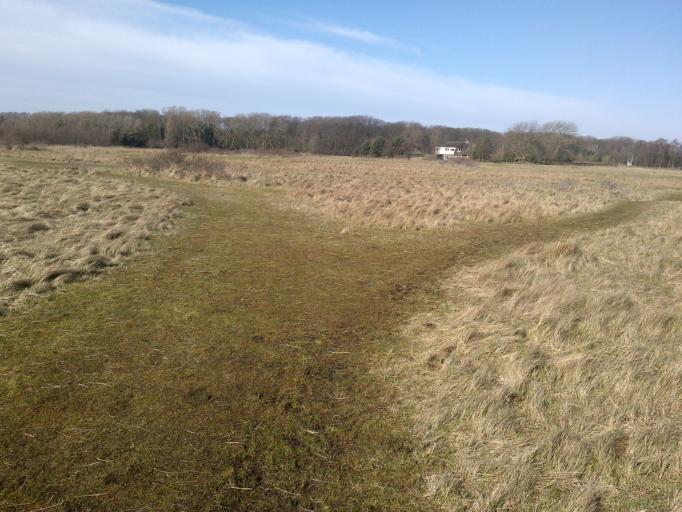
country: NL
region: South Holland
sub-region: Gemeente Wassenaar
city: Wassenaar
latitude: 52.1696
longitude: 4.3974
